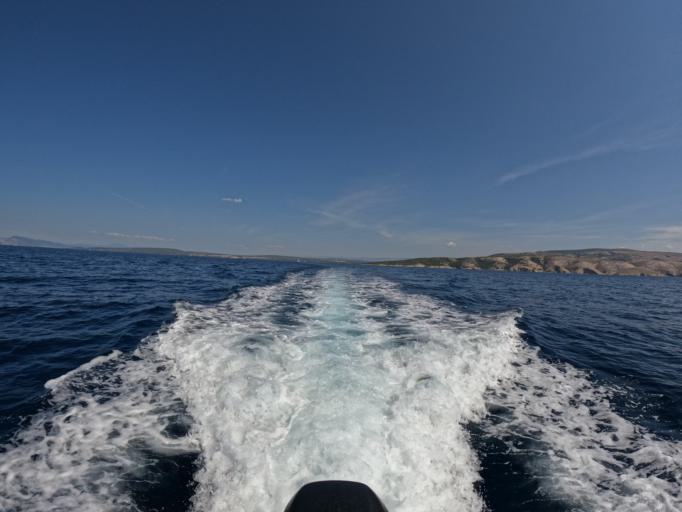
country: HR
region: Primorsko-Goranska
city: Punat
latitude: 44.9523
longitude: 14.6119
